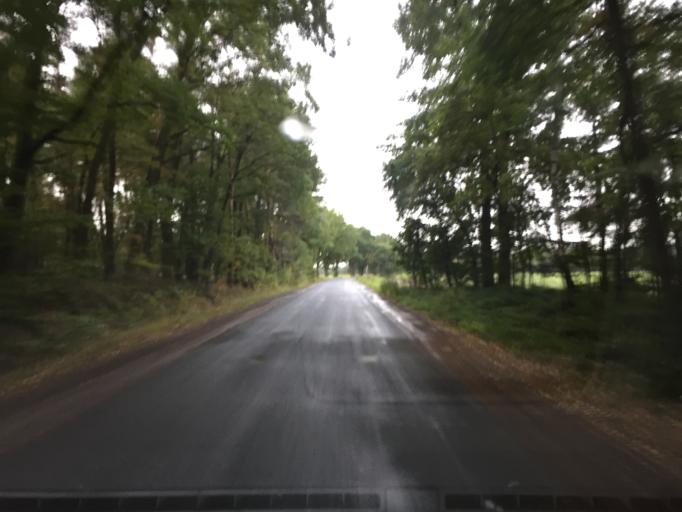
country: DE
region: Lower Saxony
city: Liebenau
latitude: 52.6350
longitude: 9.1009
